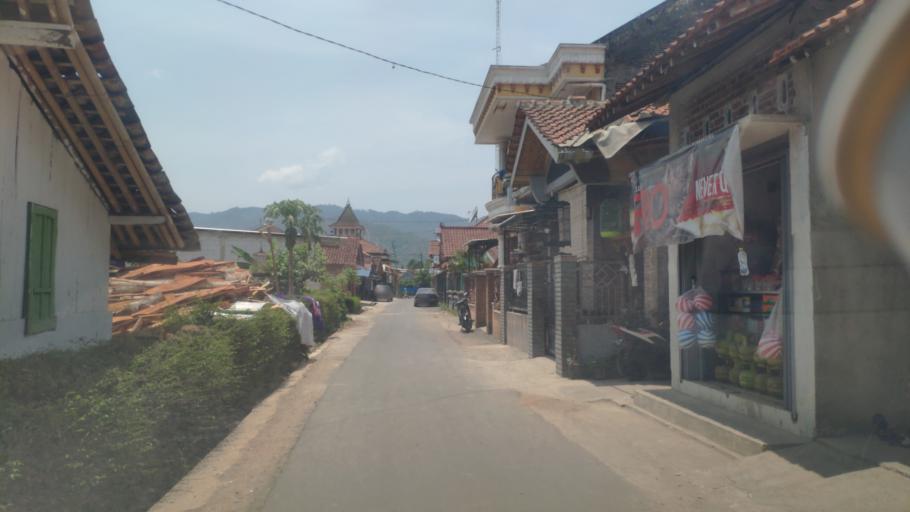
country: ID
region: Central Java
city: Wonosobo
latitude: -7.3911
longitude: 109.7066
